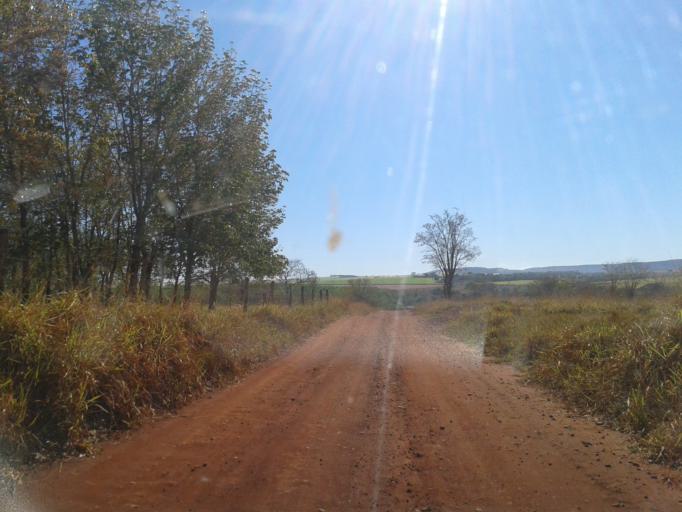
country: BR
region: Minas Gerais
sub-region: Centralina
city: Centralina
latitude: -18.5714
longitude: -49.1357
